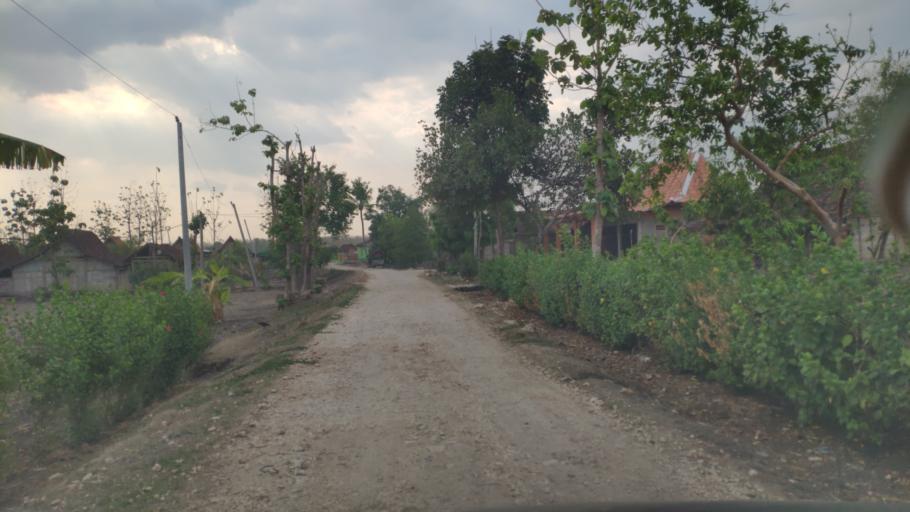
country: ID
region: Central Java
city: Randublatung
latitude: -7.2851
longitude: 111.2773
